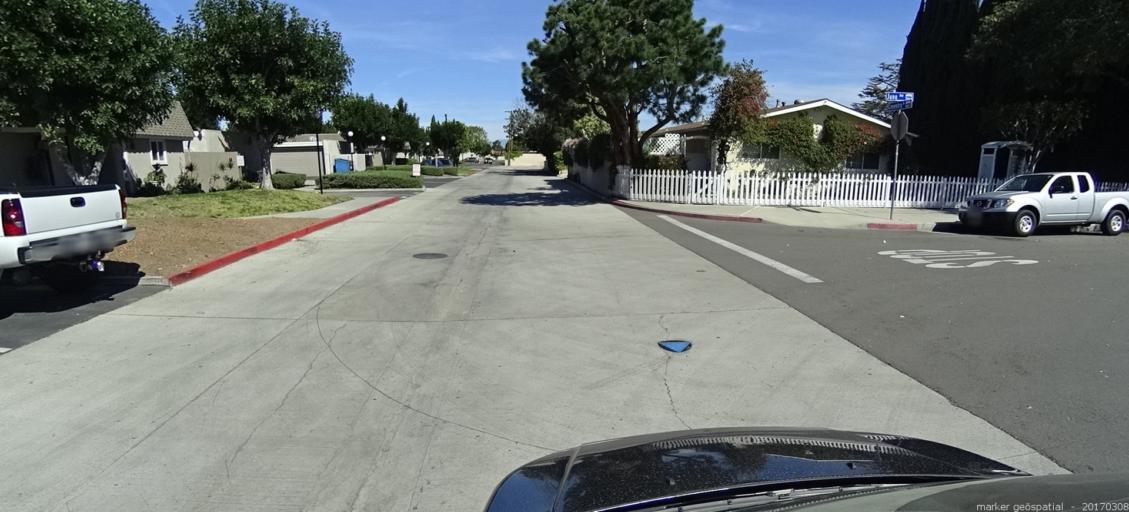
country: US
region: California
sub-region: Orange County
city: Stanton
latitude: 33.8187
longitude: -117.9567
